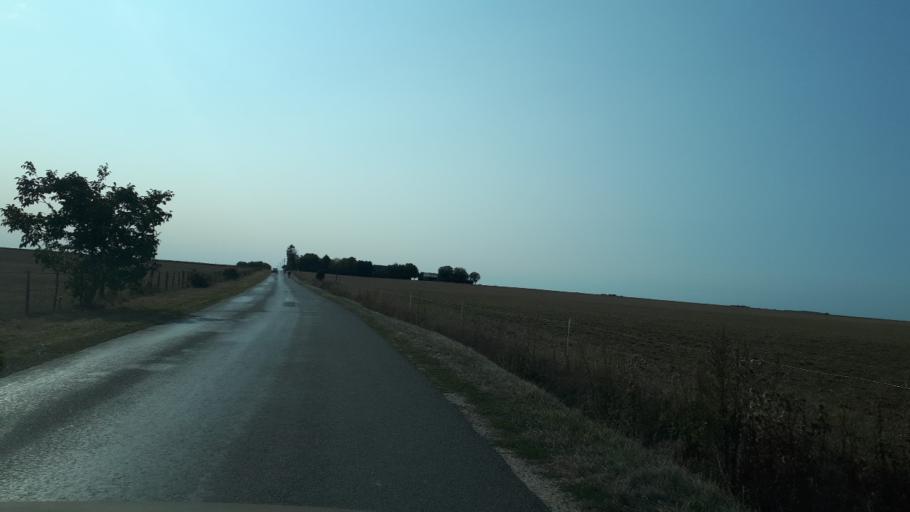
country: FR
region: Centre
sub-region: Departement du Cher
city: Rians
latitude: 47.1851
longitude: 2.7005
